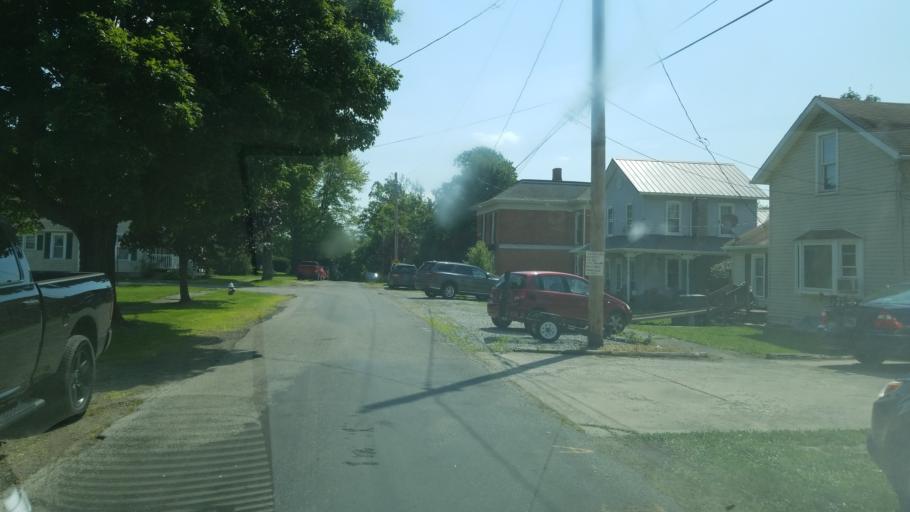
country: US
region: Ohio
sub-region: Huron County
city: Plymouth
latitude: 40.9670
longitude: -82.6026
